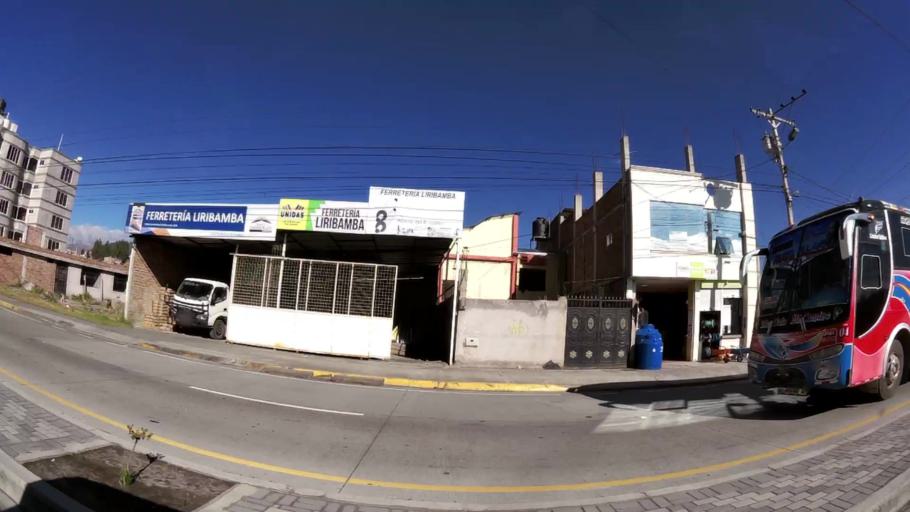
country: EC
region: Chimborazo
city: Riobamba
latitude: -1.6502
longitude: -78.6903
